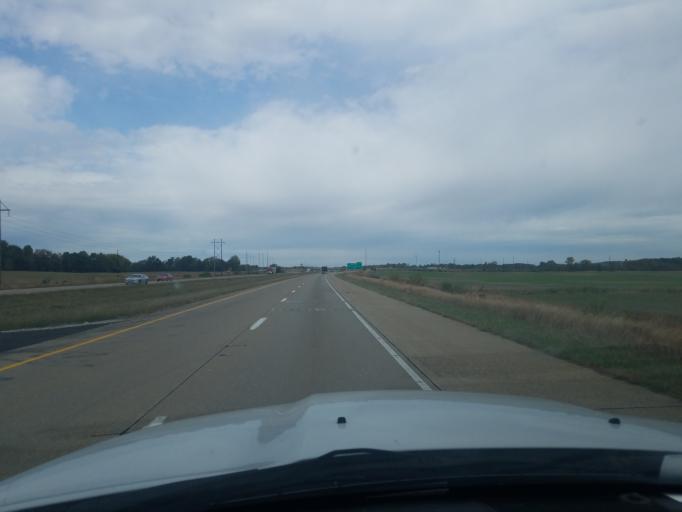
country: US
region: Indiana
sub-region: Vanderburgh County
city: Melody Hill
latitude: 38.0809
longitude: -87.4765
